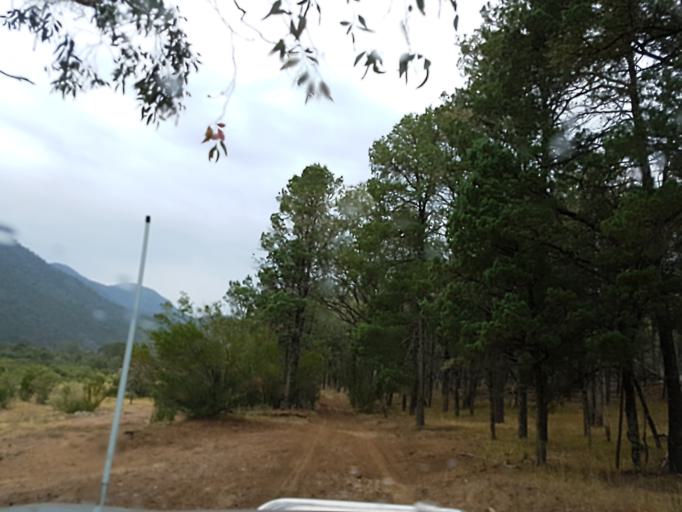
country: AU
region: New South Wales
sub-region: Snowy River
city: Jindabyne
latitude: -36.9489
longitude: 148.3985
